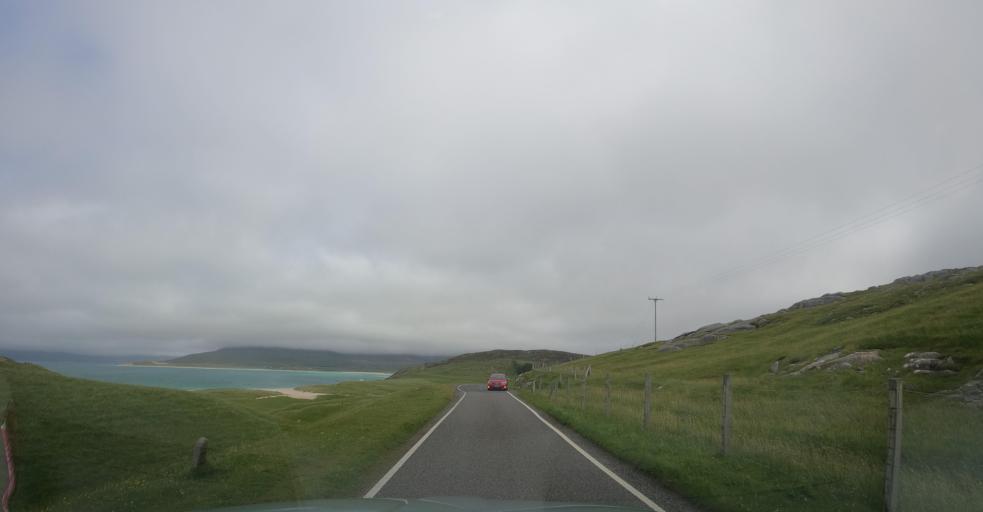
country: GB
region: Scotland
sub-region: Eilean Siar
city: Harris
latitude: 57.8615
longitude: -6.9855
